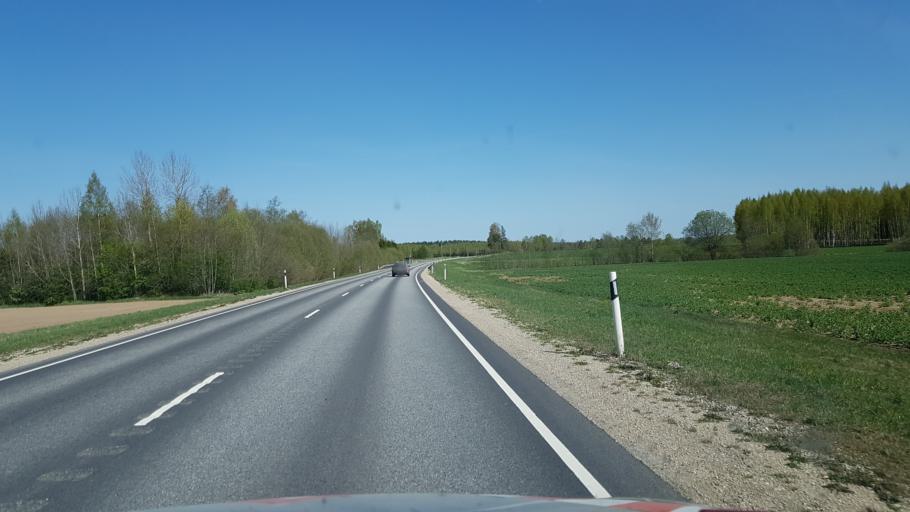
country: EE
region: Valgamaa
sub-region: Valga linn
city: Valga
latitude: 57.8951
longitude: 26.1663
